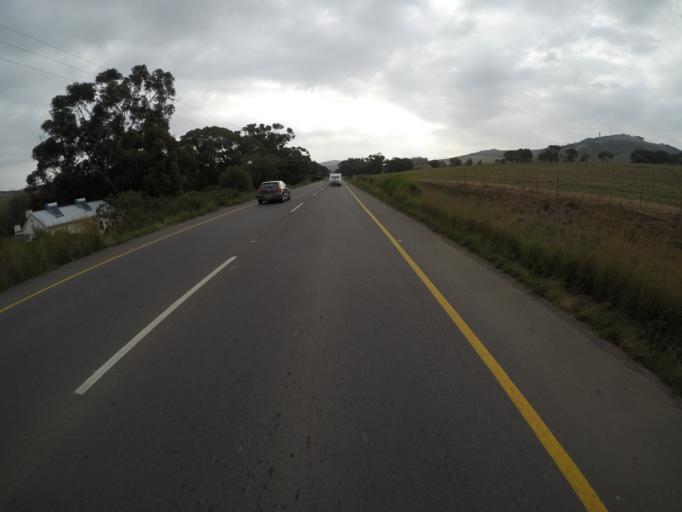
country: ZA
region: Western Cape
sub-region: City of Cape Town
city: Kraaifontein
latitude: -33.8421
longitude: 18.6169
